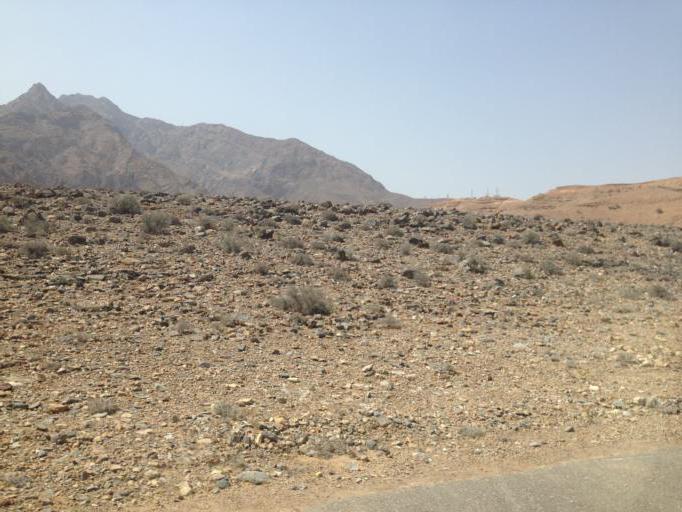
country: OM
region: Ash Sharqiyah
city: Ibra'
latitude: 23.0909
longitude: 58.8568
